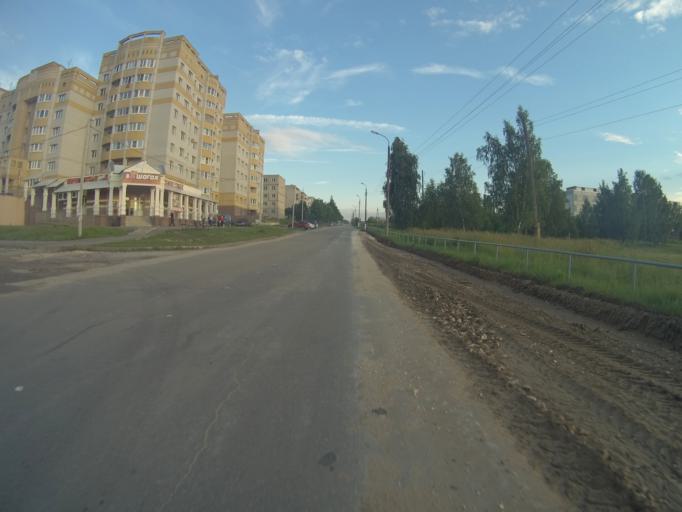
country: RU
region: Vladimir
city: Kommunar
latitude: 56.0638
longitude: 40.4876
